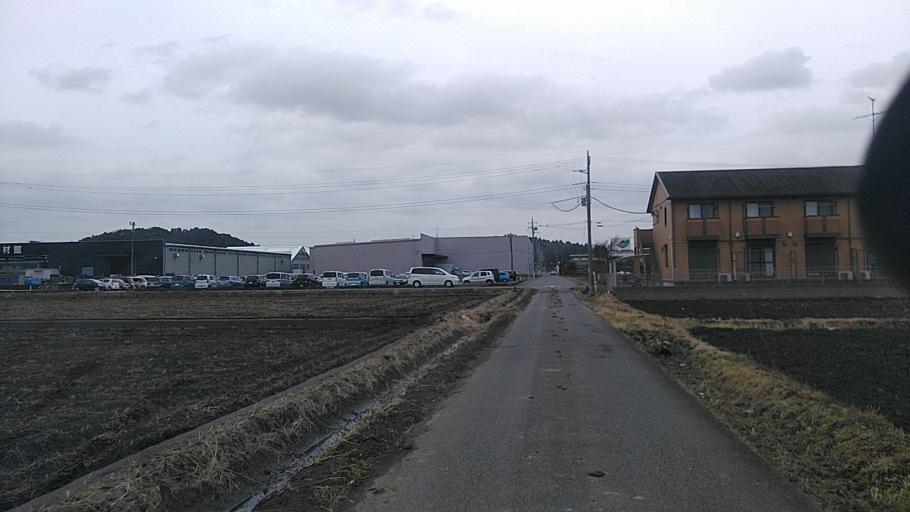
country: JP
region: Chiba
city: Togane
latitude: 35.5736
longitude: 140.3837
